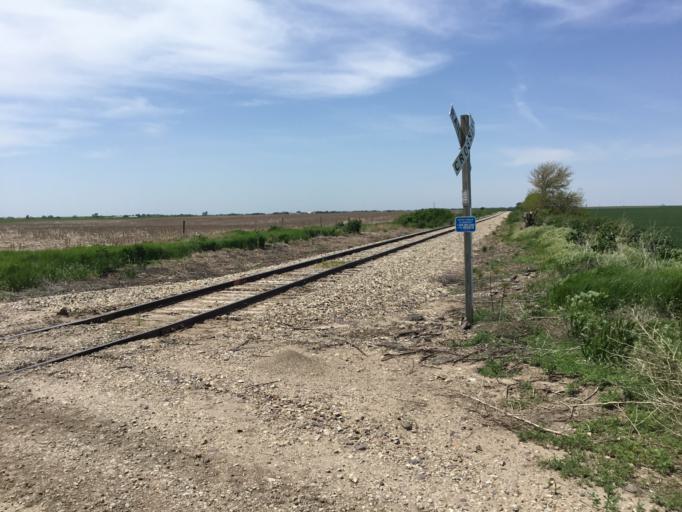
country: US
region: Kansas
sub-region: Mitchell County
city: Beloit
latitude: 39.5366
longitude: -97.9855
